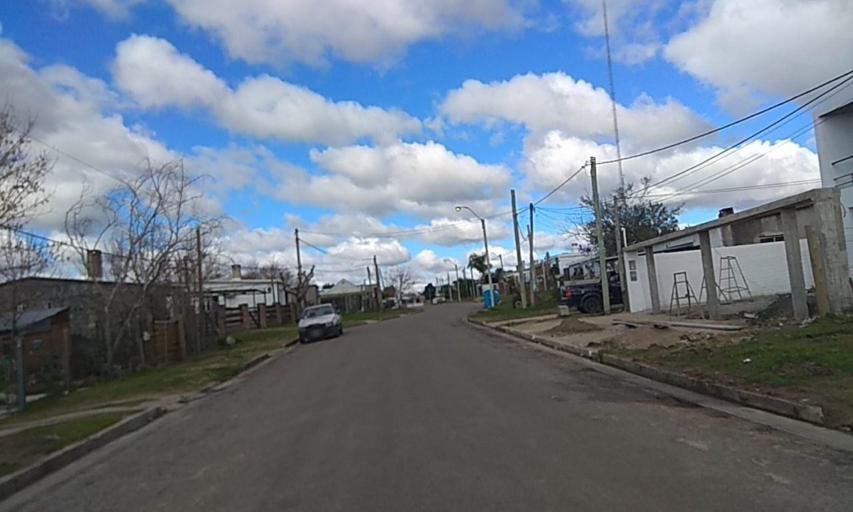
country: UY
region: Florida
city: Florida
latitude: -34.0929
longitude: -56.2356
